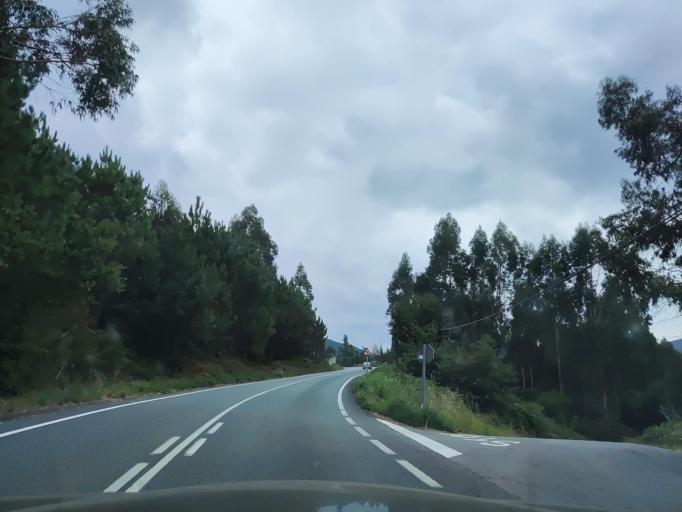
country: ES
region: Galicia
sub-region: Provincia da Coruna
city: Padron
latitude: 42.7385
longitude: -8.6288
